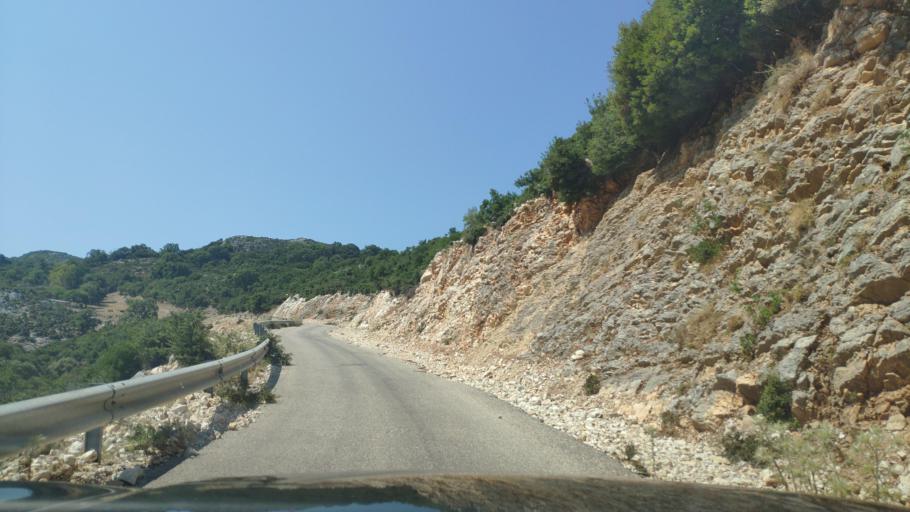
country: GR
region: West Greece
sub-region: Nomos Aitolias kai Akarnanias
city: Monastirakion
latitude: 38.8292
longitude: 20.9286
